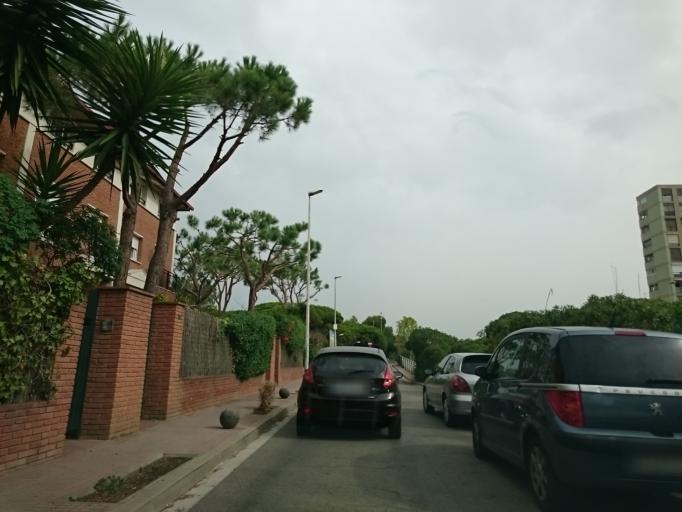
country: ES
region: Catalonia
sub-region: Provincia de Barcelona
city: Gava
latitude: 41.2681
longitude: 2.0105
